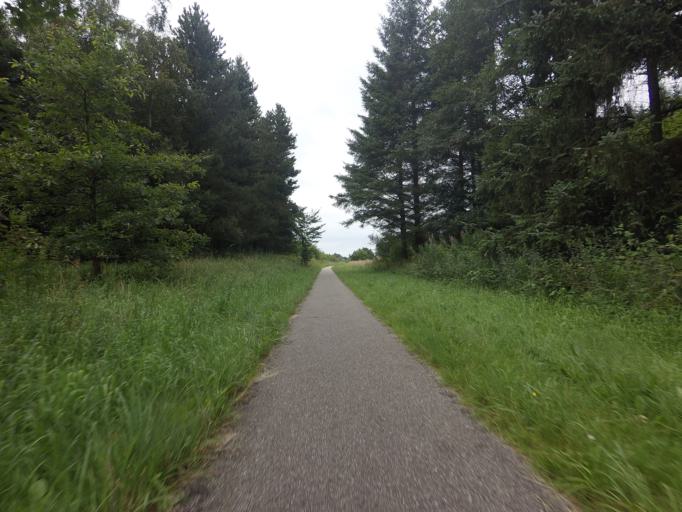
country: DK
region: Central Jutland
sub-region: Horsens Kommune
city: Braedstrup
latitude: 56.0252
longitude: 9.5477
